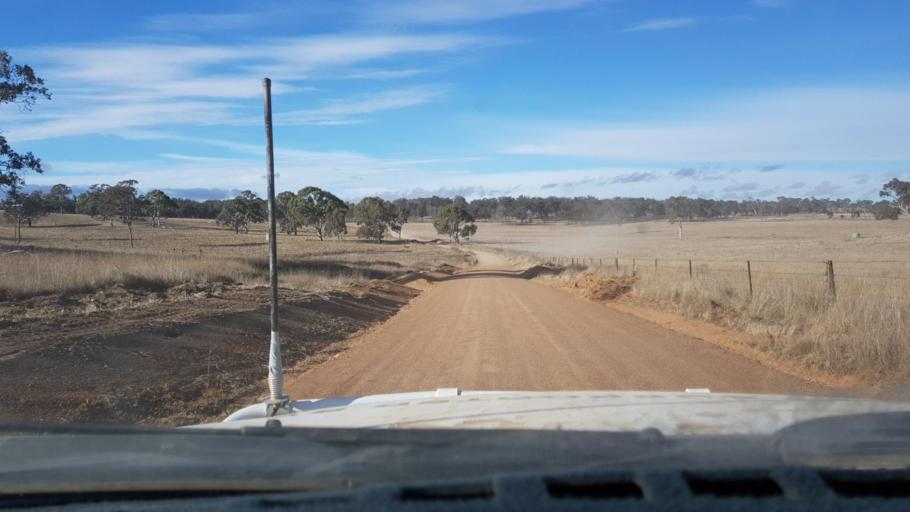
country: AU
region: New South Wales
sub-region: Armidale Dumaresq
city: Enmore
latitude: -30.7365
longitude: 151.5988
